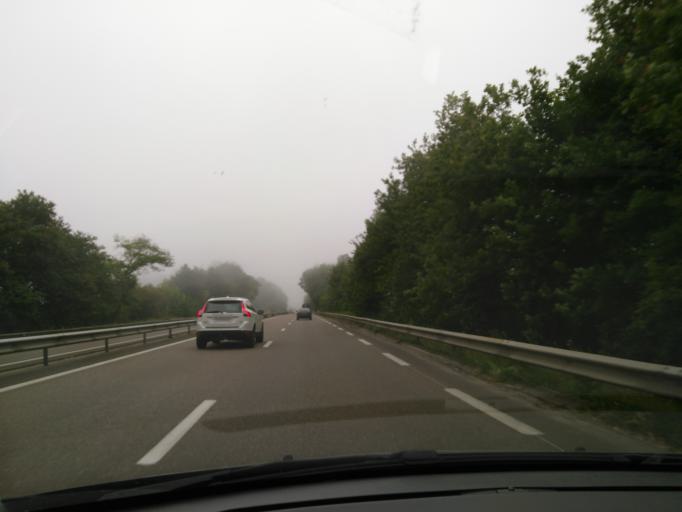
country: FR
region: Aquitaine
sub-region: Departement des Landes
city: Tartas
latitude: 43.8249
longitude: -0.8232
